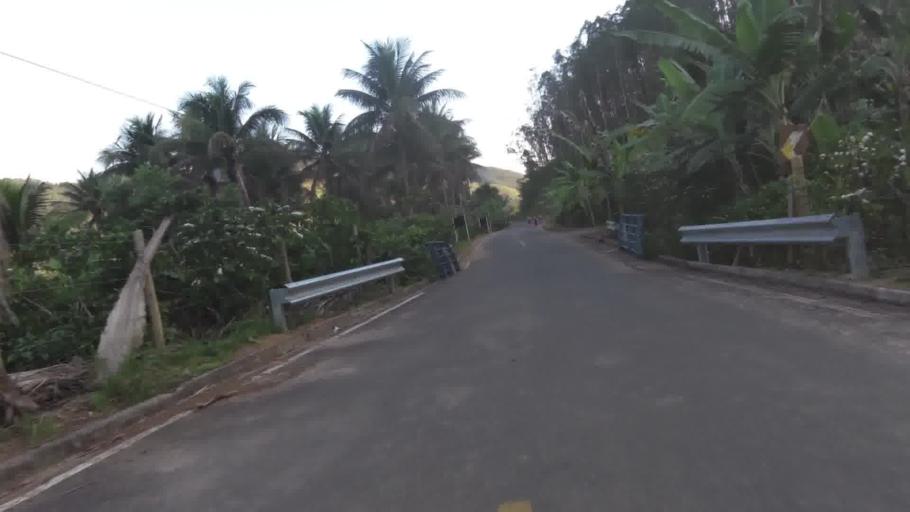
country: BR
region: Espirito Santo
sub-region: Alfredo Chaves
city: Alfredo Chaves
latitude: -20.5968
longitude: -40.7083
